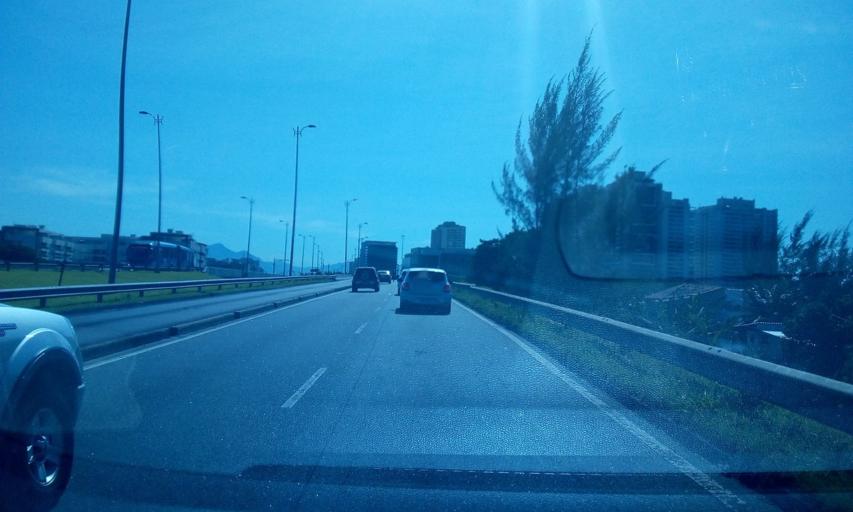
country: BR
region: Rio de Janeiro
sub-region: Nilopolis
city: Nilopolis
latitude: -23.0212
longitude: -43.4948
